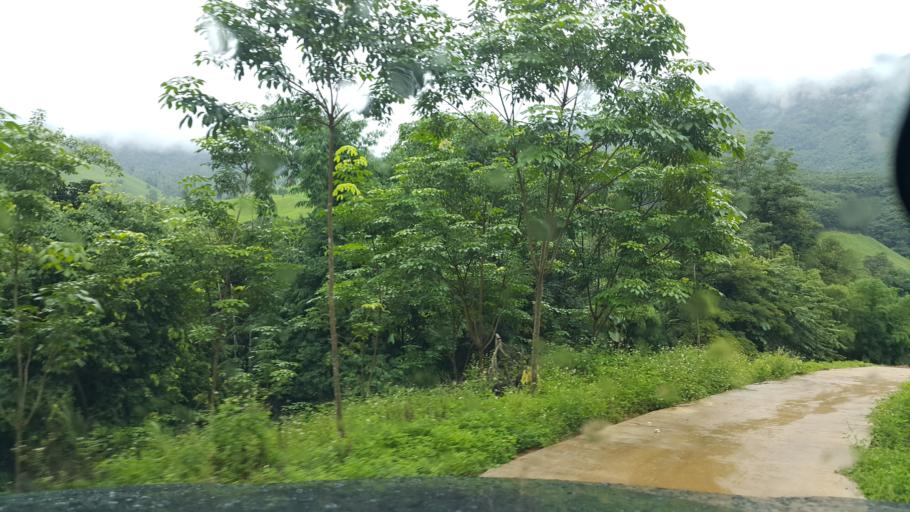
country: TH
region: Phayao
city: Chiang Kham
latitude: 19.4972
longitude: 100.4637
